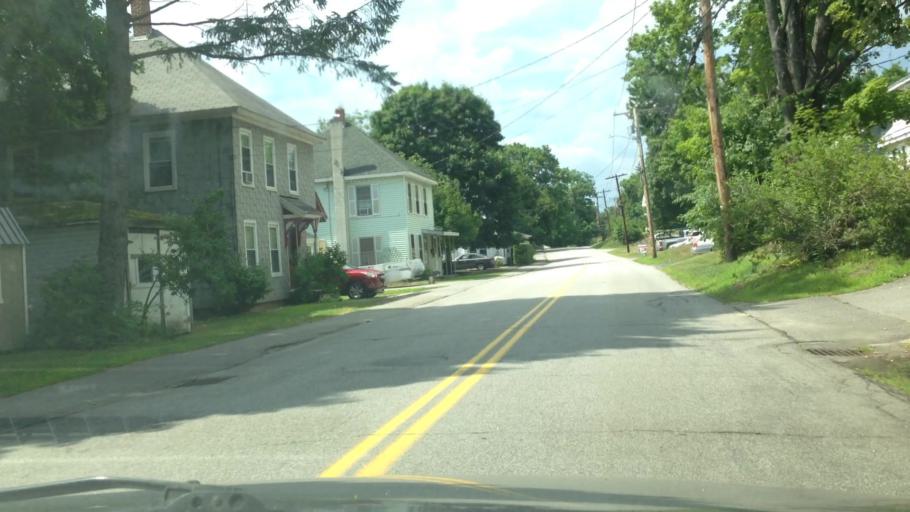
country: US
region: New Hampshire
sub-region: Cheshire County
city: Keene
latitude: 42.9259
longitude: -72.2628
